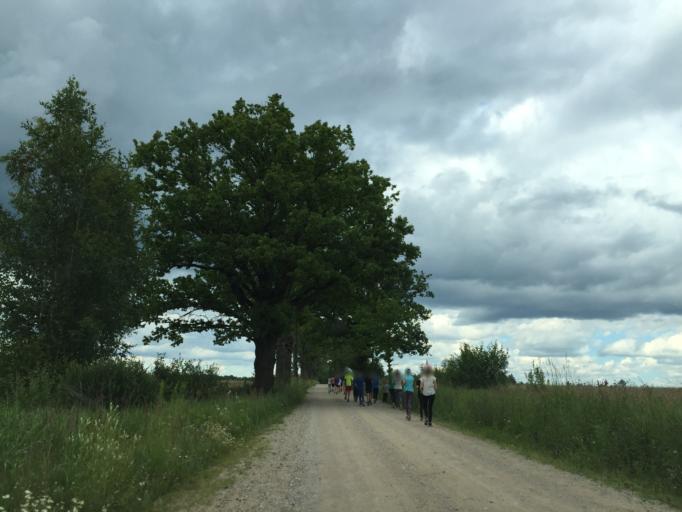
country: LV
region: Malpils
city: Malpils
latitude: 56.9172
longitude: 25.0019
